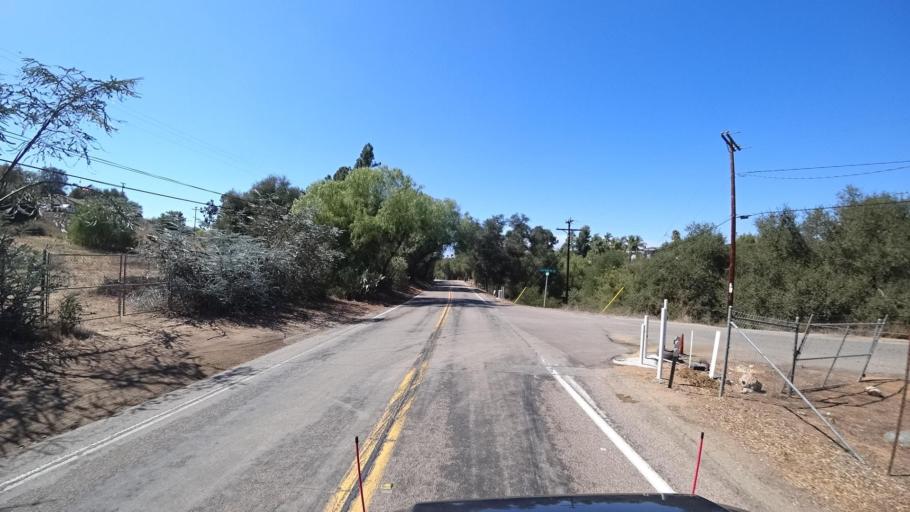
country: US
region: California
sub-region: San Diego County
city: Hidden Meadows
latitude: 33.2819
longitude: -117.1152
